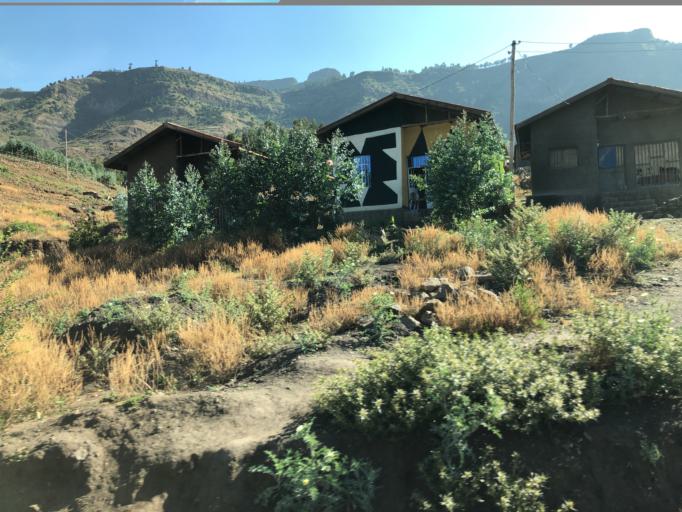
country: ET
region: Amhara
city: Lalibela
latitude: 12.0138
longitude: 39.0527
